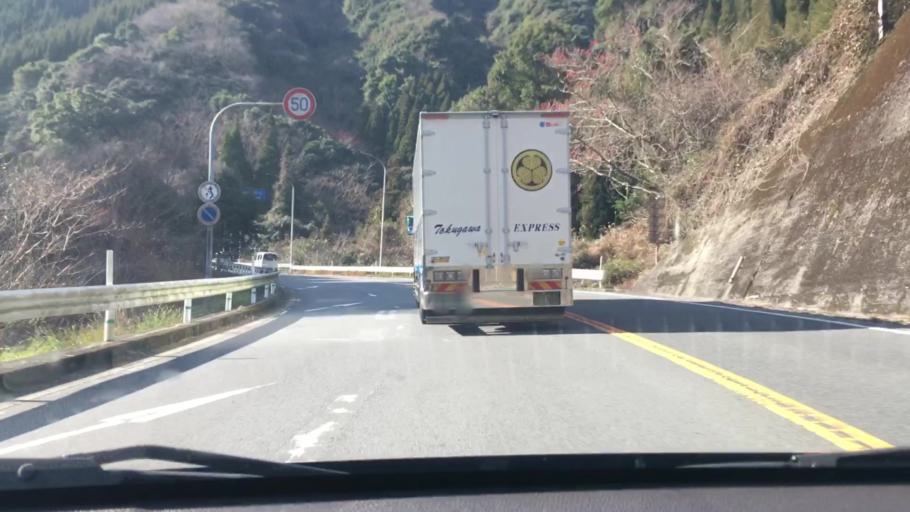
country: JP
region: Oita
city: Tsukumiura
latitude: 32.9989
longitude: 131.7825
